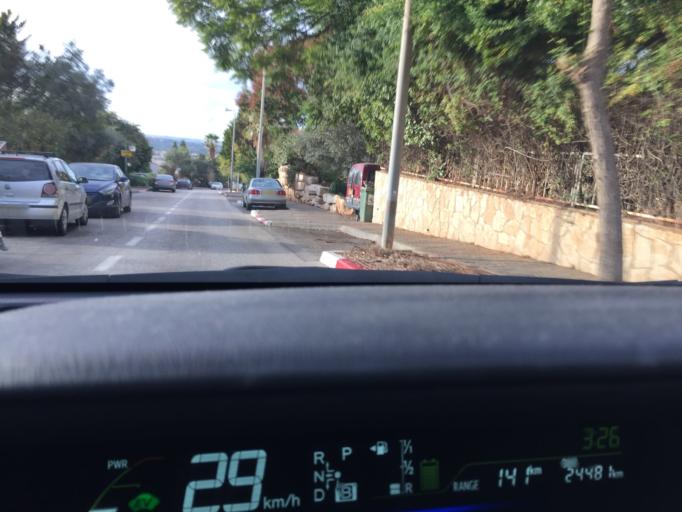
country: PS
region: West Bank
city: Az Zawiyah
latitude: 32.1086
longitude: 35.0333
